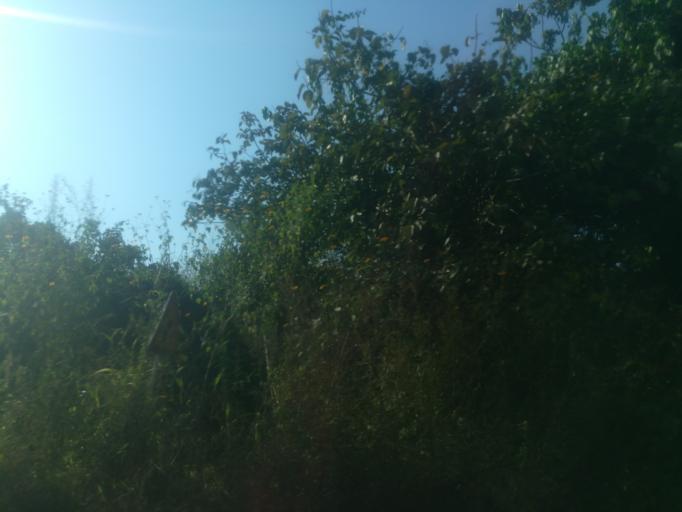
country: NG
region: Ogun
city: Abeokuta
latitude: 7.1462
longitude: 3.2567
